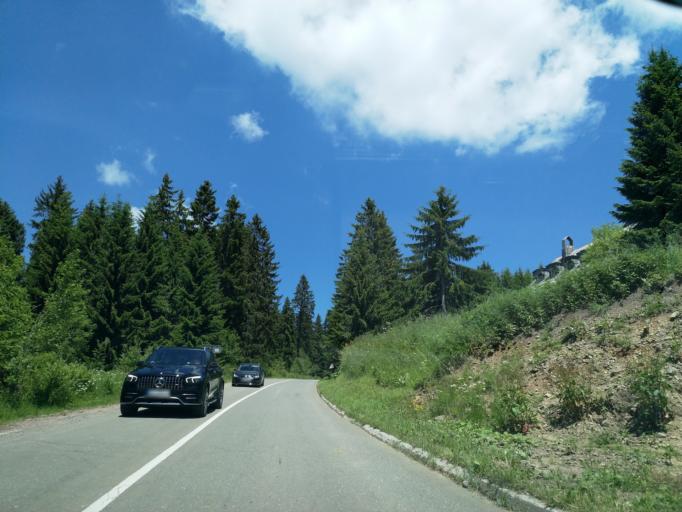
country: XK
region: Mitrovica
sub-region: Komuna e Leposaviqit
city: Leposaviq
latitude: 43.2790
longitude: 20.7952
